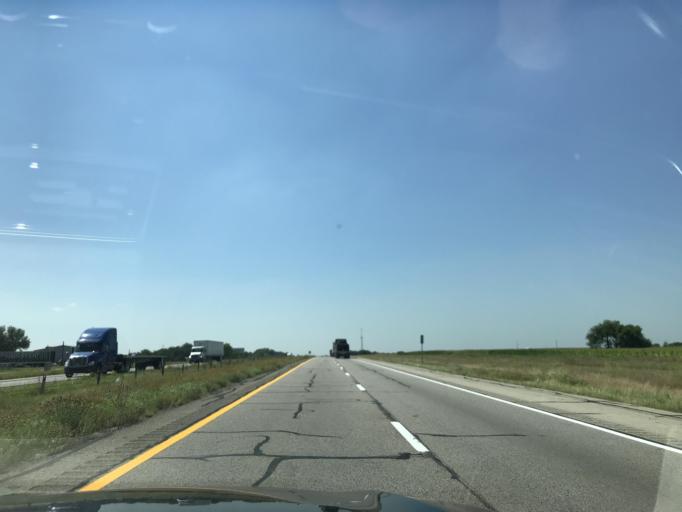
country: US
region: Texas
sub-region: Johnson County
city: Alvarado
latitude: 32.3435
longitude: -97.1935
